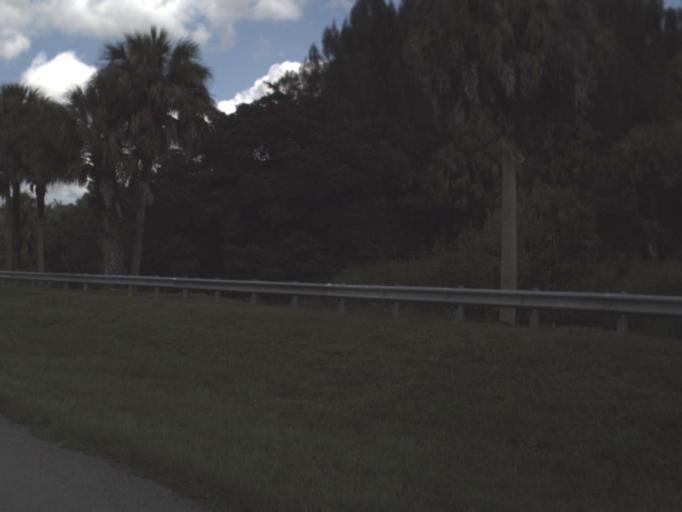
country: US
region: Florida
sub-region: Collier County
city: Immokalee
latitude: 26.2958
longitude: -81.3426
